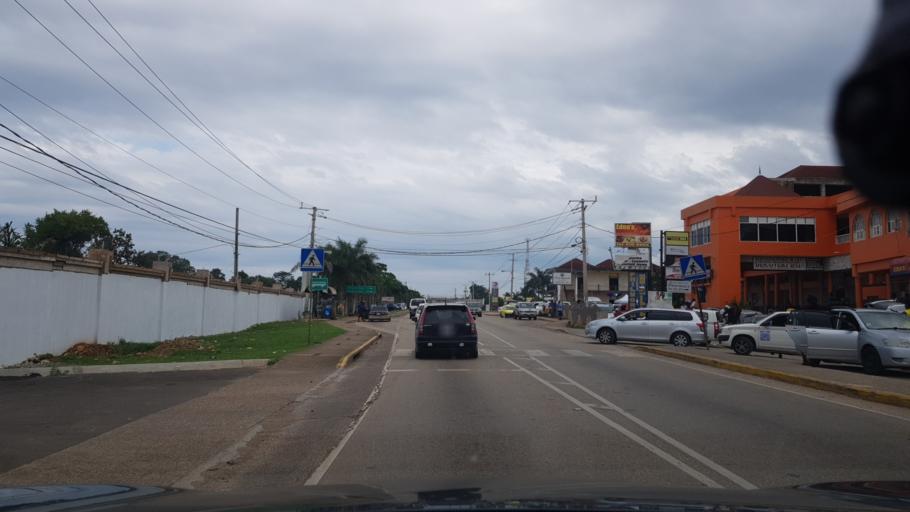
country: JM
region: Saint Ann
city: Discovery Bay
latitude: 18.4602
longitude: -77.4007
